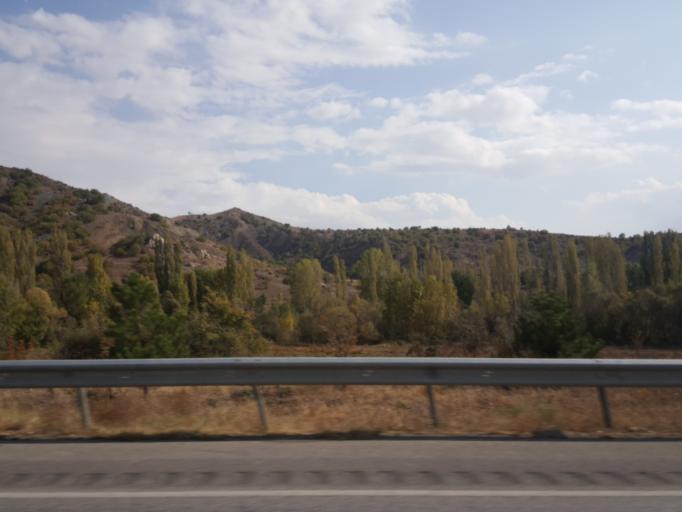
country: TR
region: Corum
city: Sungurlu
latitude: 40.1957
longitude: 34.5082
